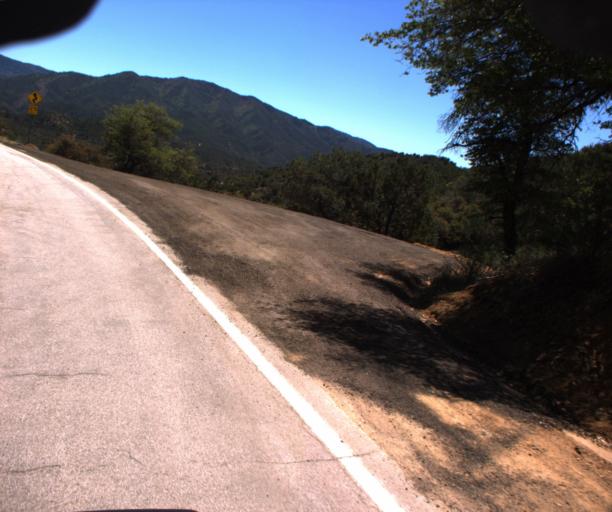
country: US
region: Arizona
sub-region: Yavapai County
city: Prescott
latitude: 34.4472
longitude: -112.5421
